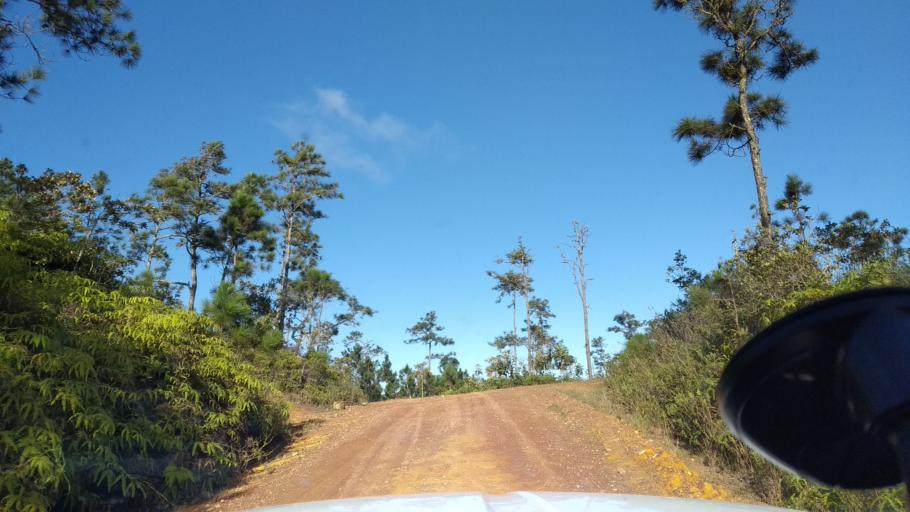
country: BZ
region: Cayo
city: Belmopan
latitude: 16.9992
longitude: -88.8472
